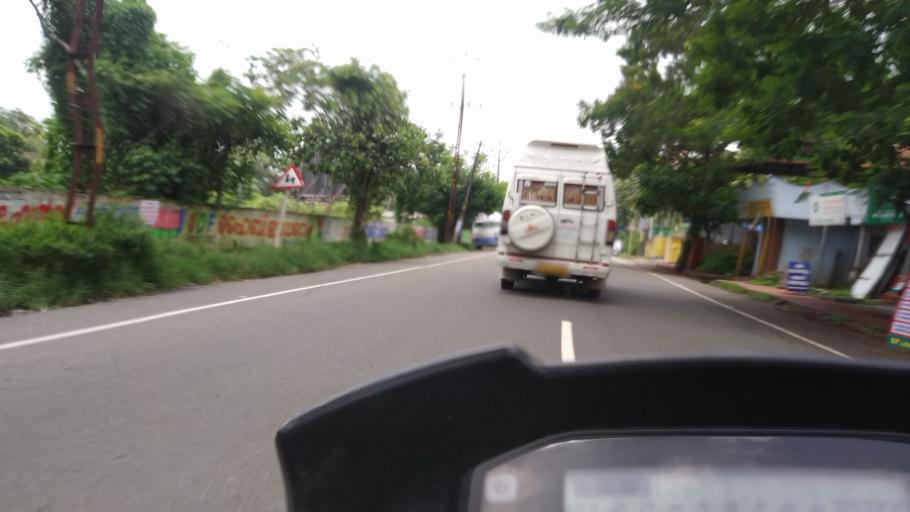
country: IN
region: Kerala
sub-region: Ernakulam
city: Elur
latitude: 10.1368
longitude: 76.2697
